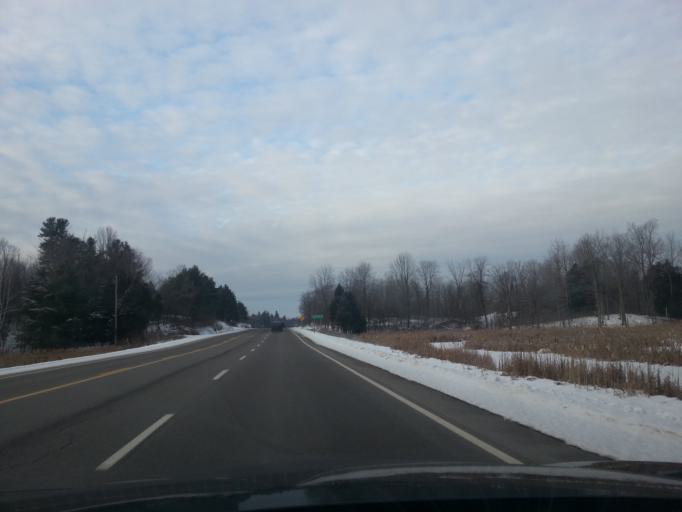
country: CA
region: Ontario
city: Perth
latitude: 44.8484
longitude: -76.4758
